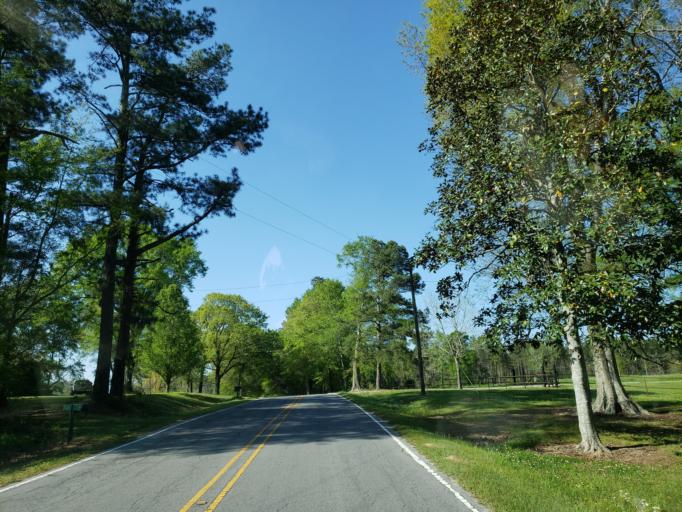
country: US
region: Mississippi
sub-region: Forrest County
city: Rawls Springs
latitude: 31.5031
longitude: -89.3599
